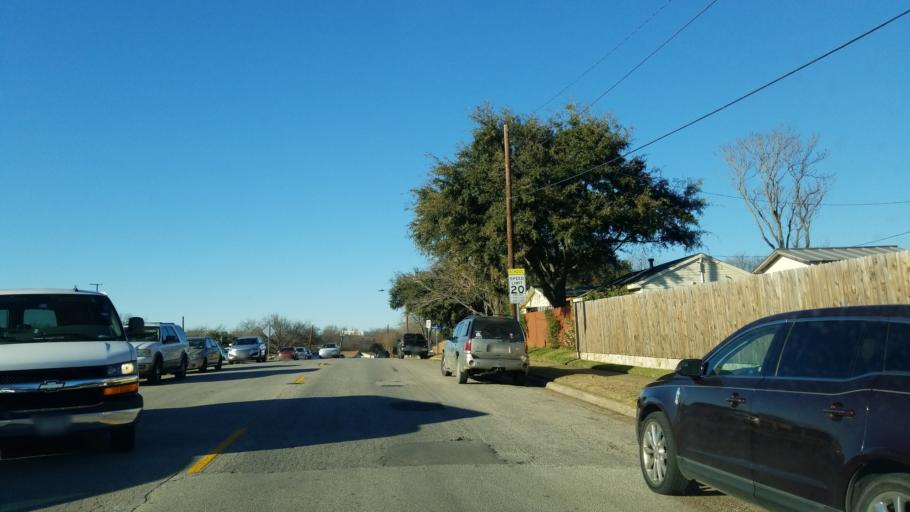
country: US
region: Texas
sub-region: Tarrant County
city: Arlington
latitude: 32.7264
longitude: -97.0677
